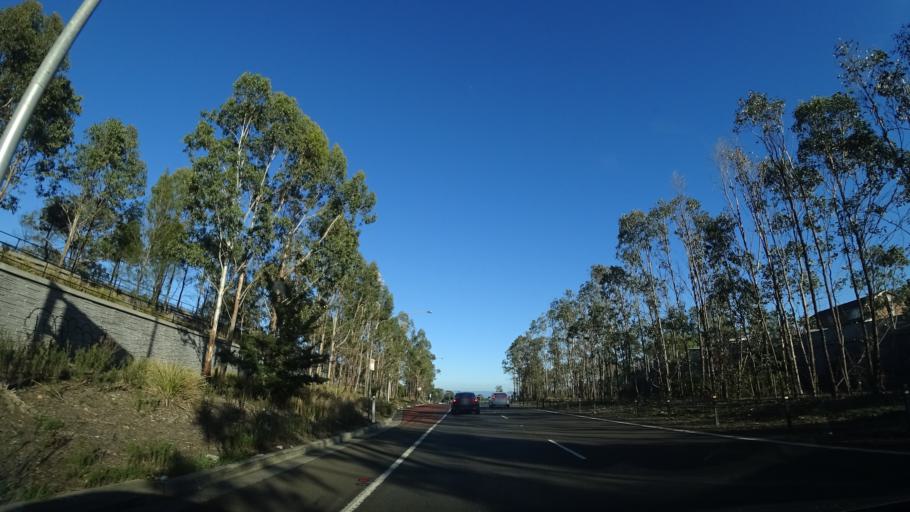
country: AU
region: New South Wales
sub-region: Blacktown
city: Rouse Hill
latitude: -33.6635
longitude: 150.8955
